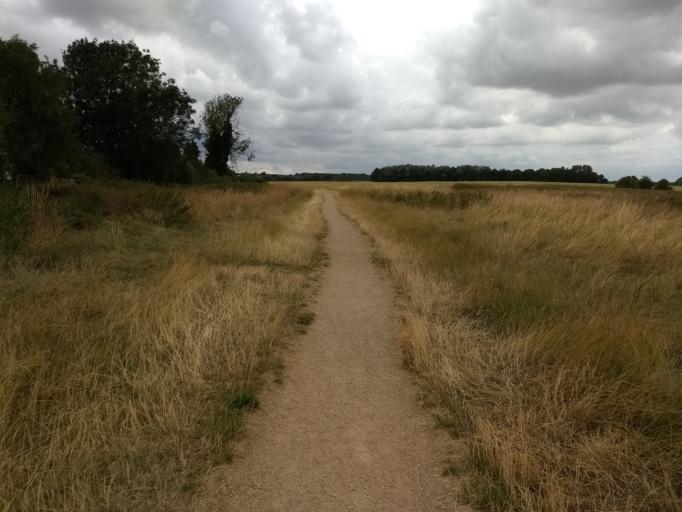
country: GB
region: England
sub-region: Milton Keynes
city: Newport Pagnell
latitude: 52.0876
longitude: -0.7270
